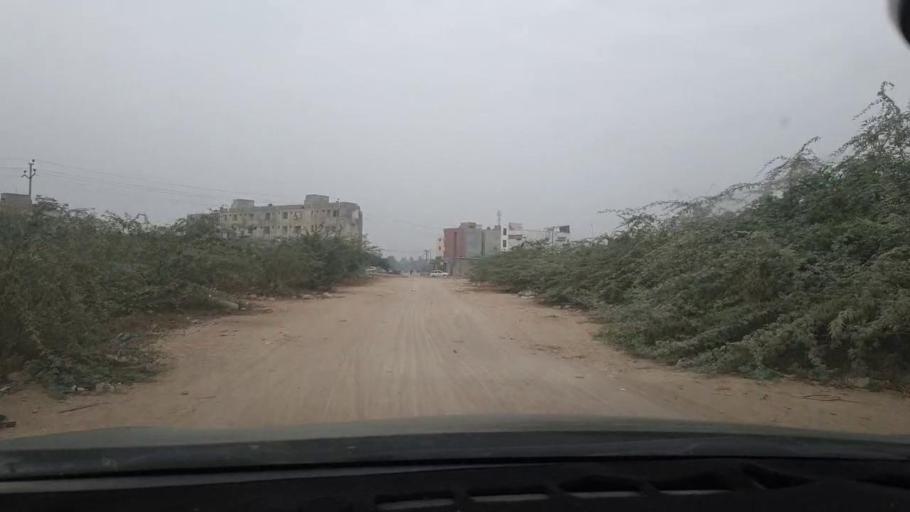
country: PK
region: Sindh
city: Malir Cantonment
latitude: 24.9209
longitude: 67.2614
